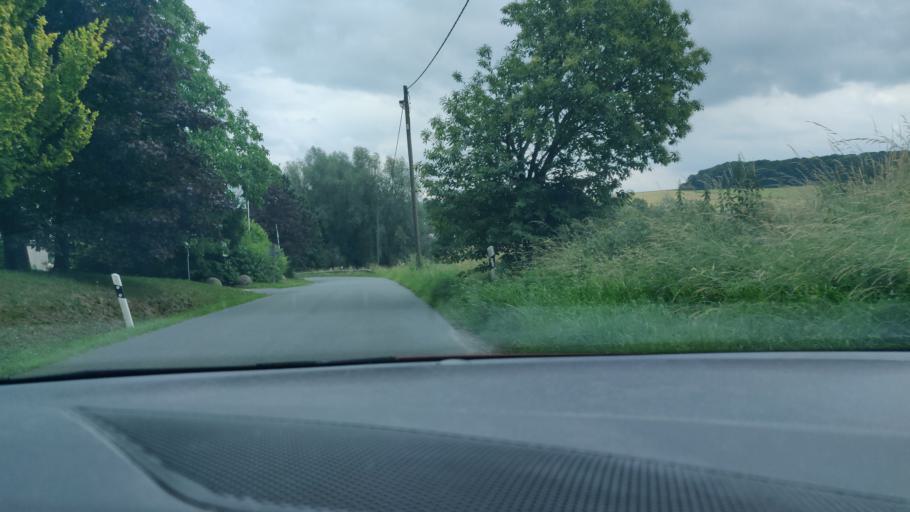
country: DE
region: North Rhine-Westphalia
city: Wulfrath
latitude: 51.2833
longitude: 7.0891
